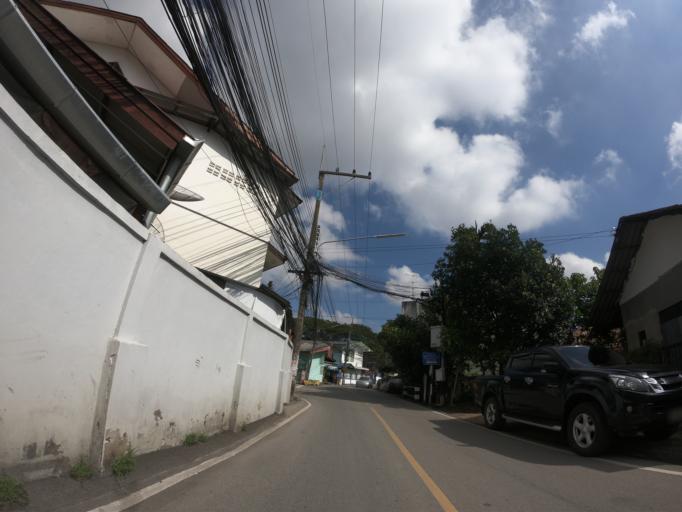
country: TH
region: Chiang Mai
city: Chiang Mai
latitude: 18.7858
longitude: 99.0310
